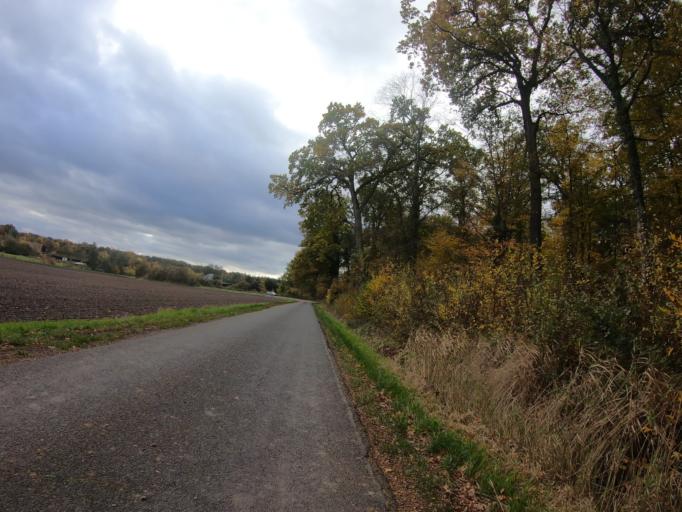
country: DE
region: Lower Saxony
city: Adenbuettel
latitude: 52.4057
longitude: 10.4728
